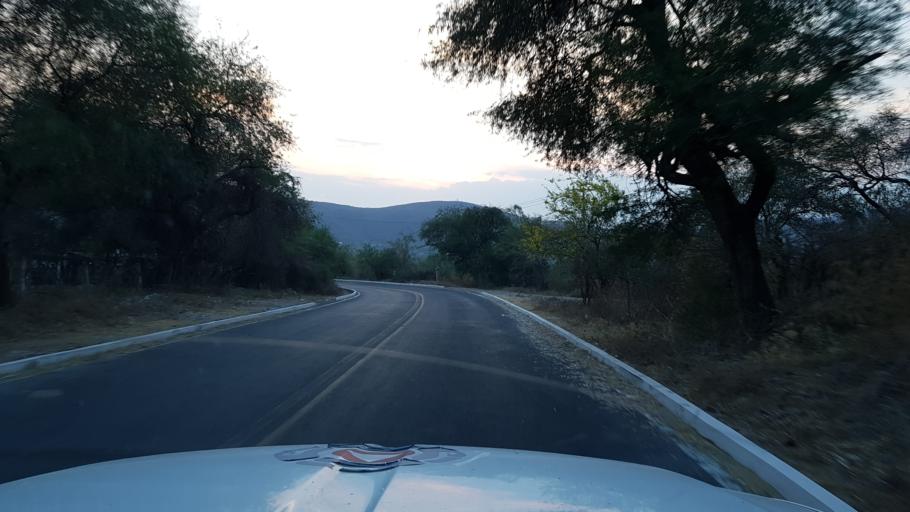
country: MX
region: Morelos
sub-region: Tlaltizapan de Zapata
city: Colonia Palo Prieto (Chipitongo)
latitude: 18.7156
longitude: -99.1061
